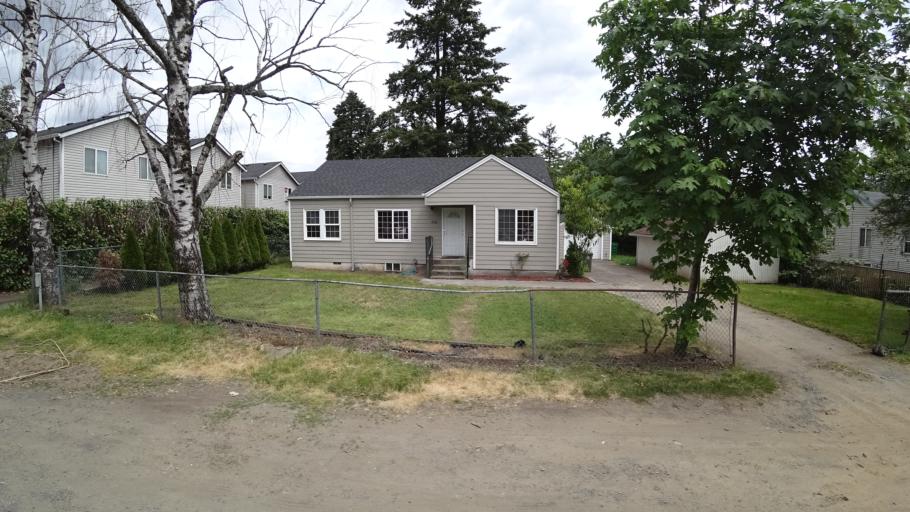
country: US
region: Oregon
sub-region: Clackamas County
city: Happy Valley
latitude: 45.4982
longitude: -122.5164
